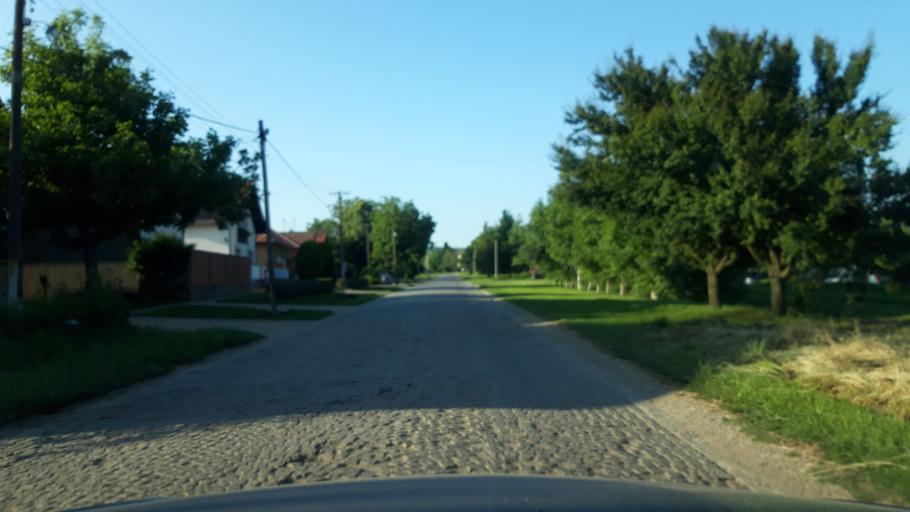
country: RS
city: Celarevo
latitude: 45.1062
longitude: 19.5028
